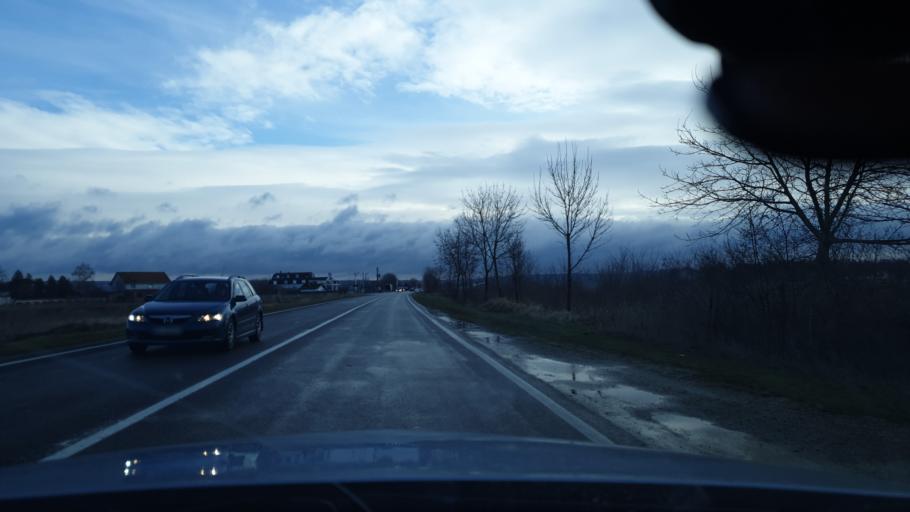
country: RS
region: Central Serbia
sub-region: Branicevski Okrug
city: Pozarevac
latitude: 44.6024
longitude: 21.1373
